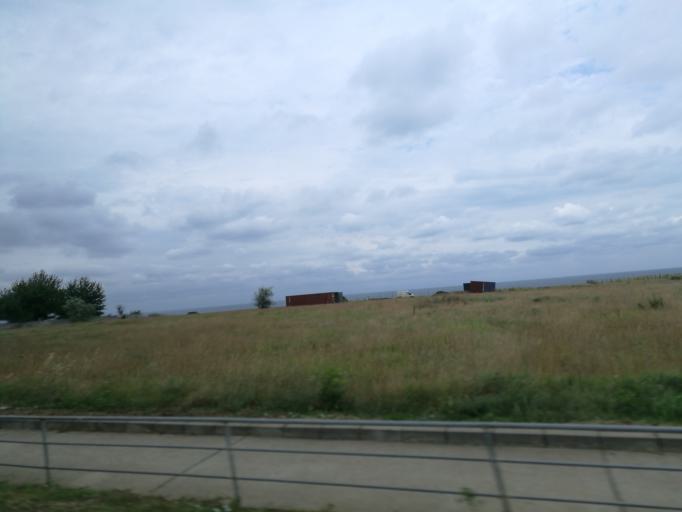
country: RO
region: Constanta
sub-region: Municipiul Mangalia
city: Mangalia
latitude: 43.7764
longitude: 28.5780
